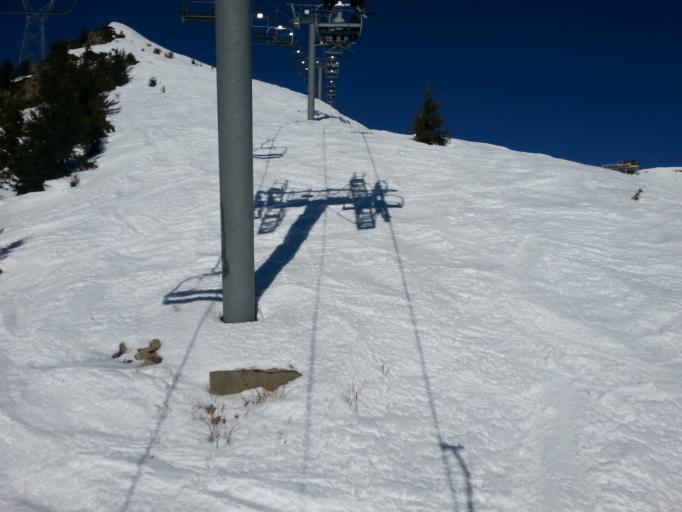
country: FR
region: Rhone-Alpes
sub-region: Departement de la Haute-Savoie
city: Samoens
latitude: 46.0274
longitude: 6.6949
